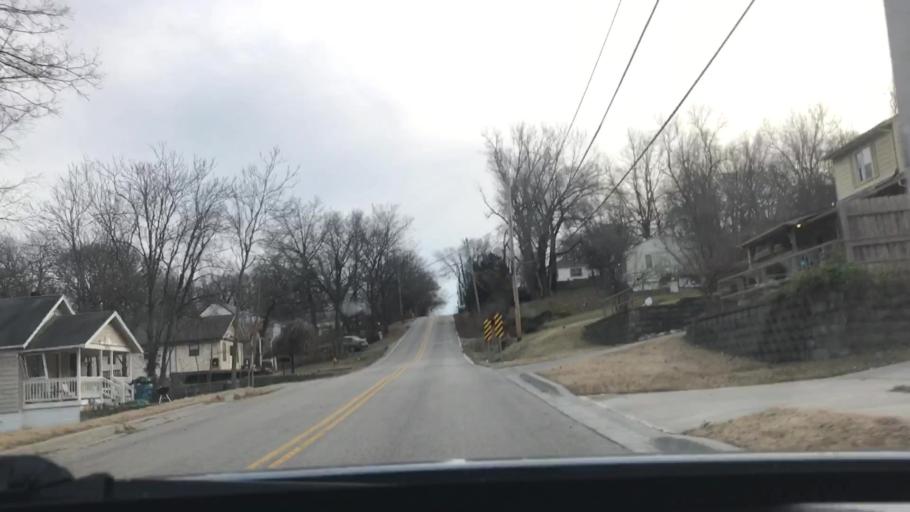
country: US
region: Missouri
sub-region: Jackson County
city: Independence
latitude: 39.0719
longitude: -94.4427
